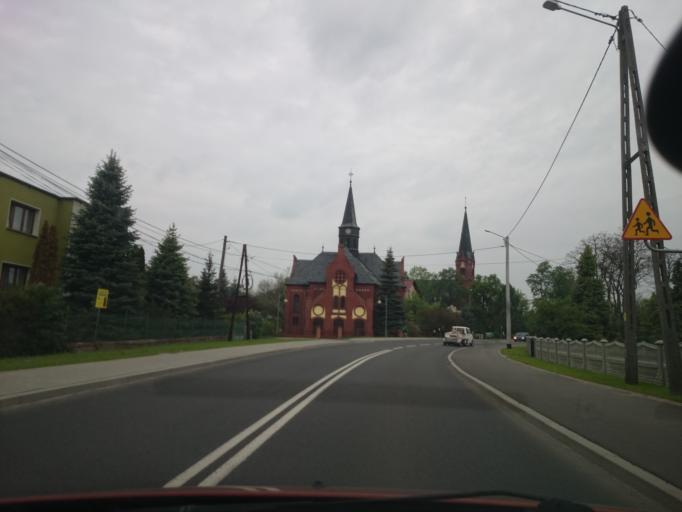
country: PL
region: Opole Voivodeship
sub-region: Powiat opolski
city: Kup
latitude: 50.8075
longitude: 17.8822
